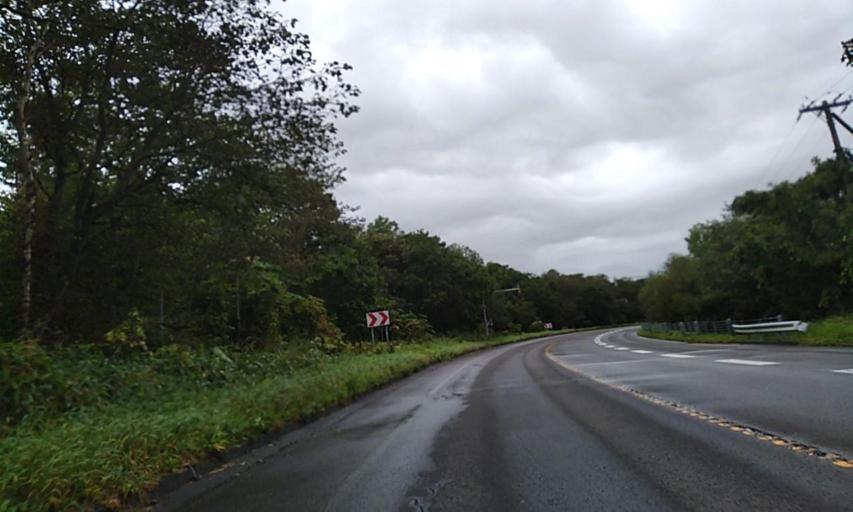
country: JP
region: Hokkaido
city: Kushiro
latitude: 42.9297
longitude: 144.0150
